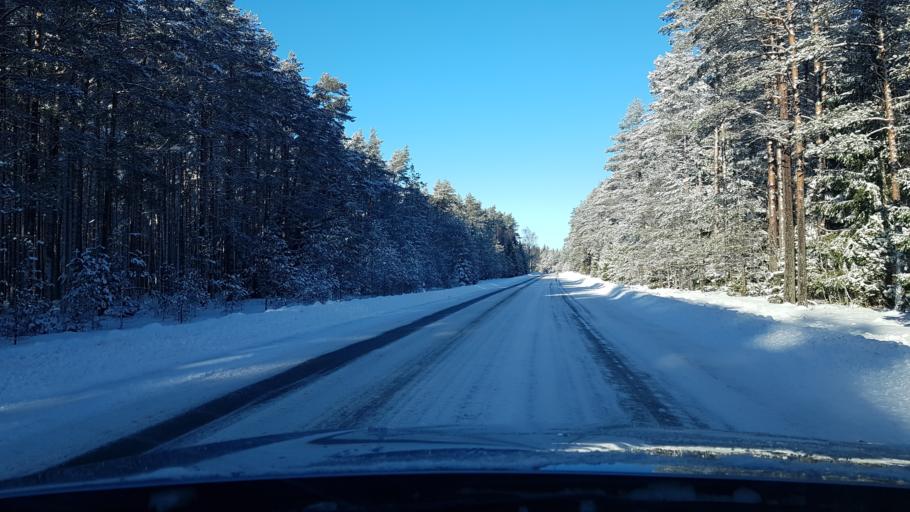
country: EE
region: Hiiumaa
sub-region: Kaerdla linn
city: Kardla
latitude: 58.9325
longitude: 22.7829
